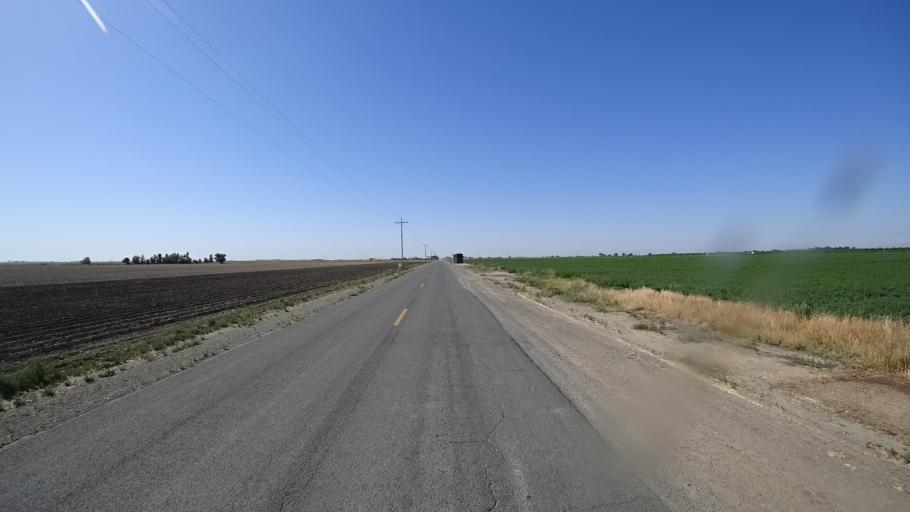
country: US
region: California
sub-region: Kings County
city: Home Garden
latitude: 36.2666
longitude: -119.5474
